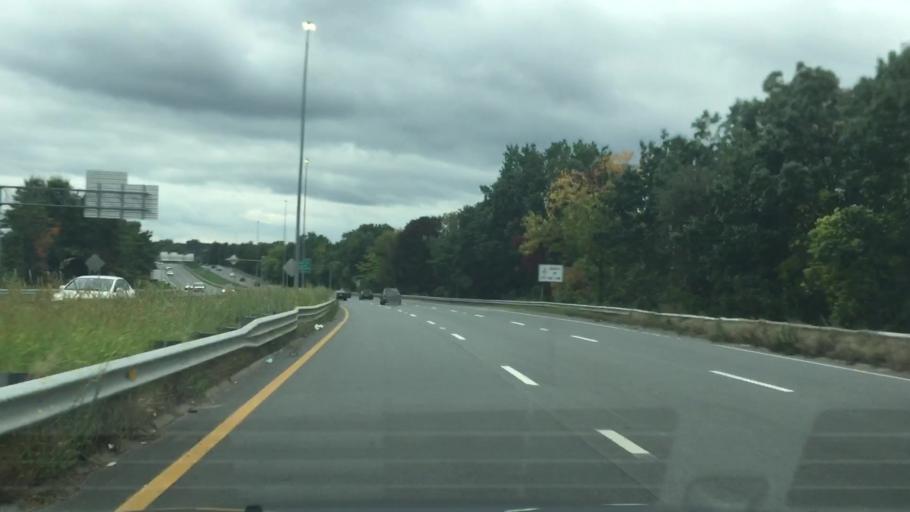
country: US
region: Massachusetts
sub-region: Middlesex County
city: Lowell
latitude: 42.6338
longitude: -71.3121
